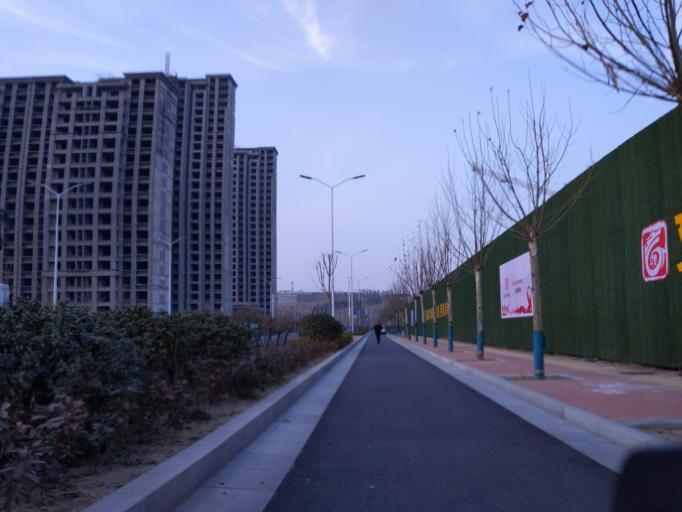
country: CN
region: Henan Sheng
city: Puyang
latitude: 35.8146
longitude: 115.0118
